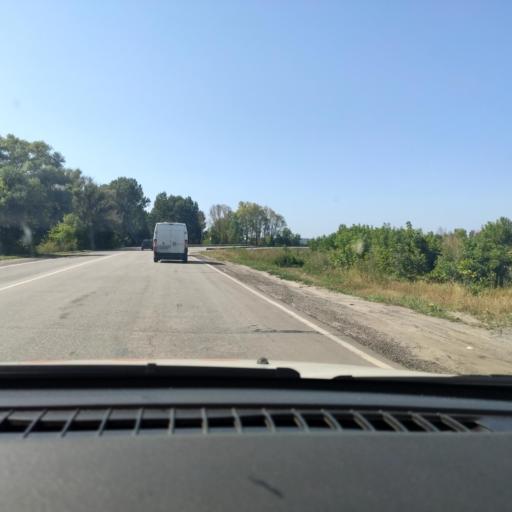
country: RU
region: Voronezj
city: Ostrogozhsk
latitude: 50.8406
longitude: 39.1218
